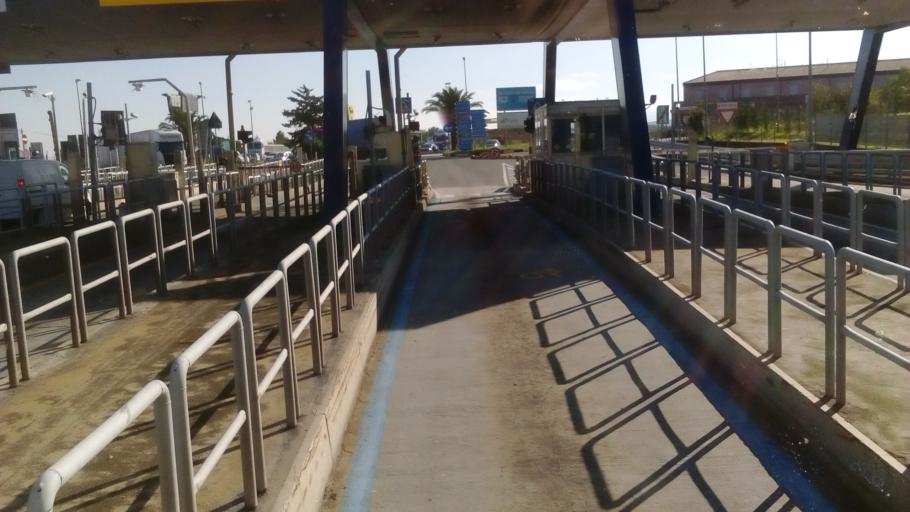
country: IT
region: Apulia
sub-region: Provincia di Foggia
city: Candela
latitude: 41.1509
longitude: 15.5260
